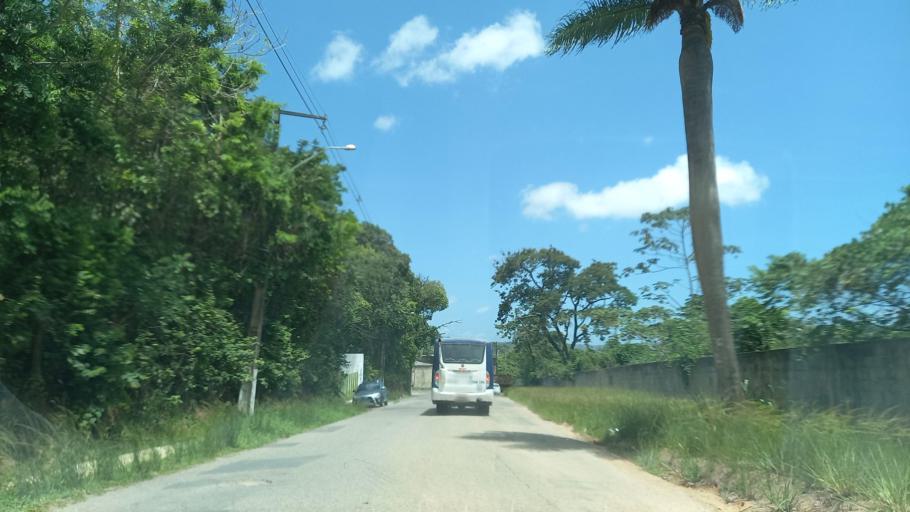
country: BR
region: Pernambuco
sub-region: Jaboatao Dos Guararapes
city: Jaboatao
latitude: -8.1629
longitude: -34.9922
